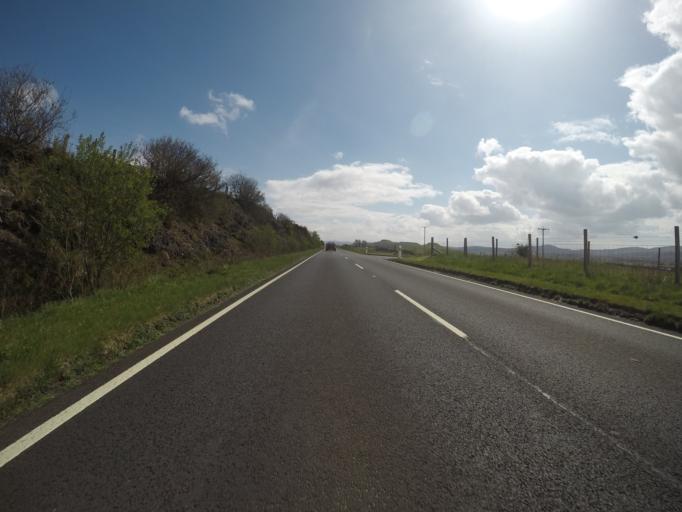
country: GB
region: Scotland
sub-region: Highland
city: Portree
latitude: 57.4965
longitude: -6.3221
